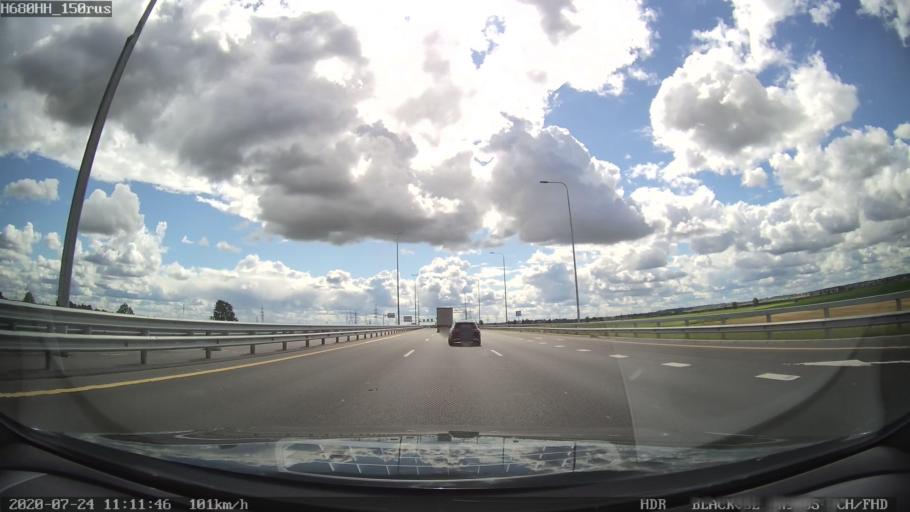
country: RU
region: Leningrad
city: Fedorovskoye
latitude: 59.7181
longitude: 30.5213
